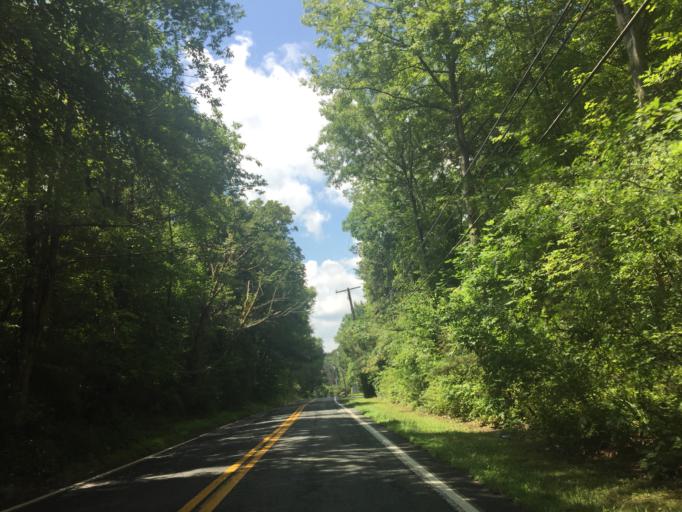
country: US
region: Maryland
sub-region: Baltimore County
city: Kingsville
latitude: 39.4353
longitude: -76.4060
